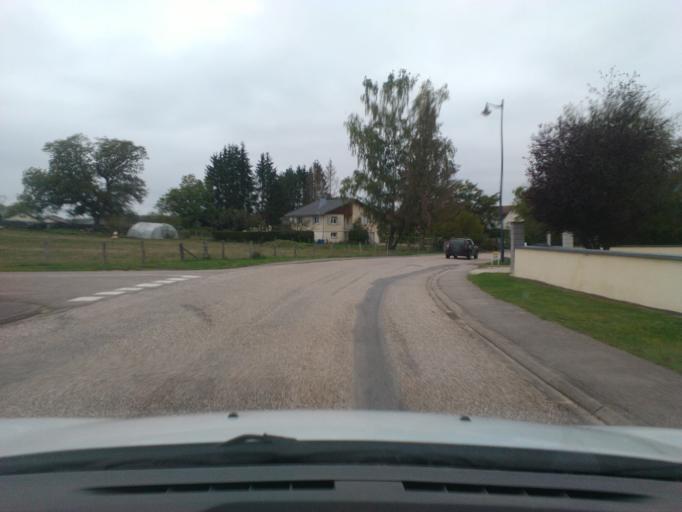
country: FR
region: Lorraine
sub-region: Departement des Vosges
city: Thaon-les-Vosges
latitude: 48.2910
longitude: 6.4453
